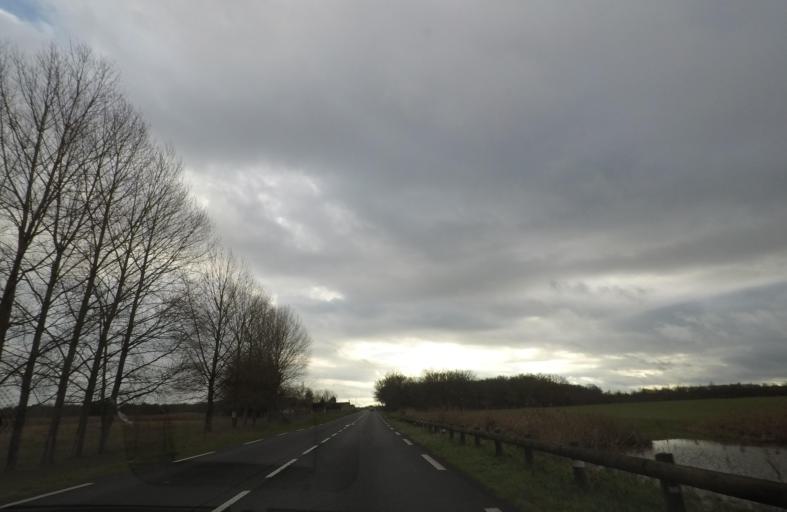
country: FR
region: Centre
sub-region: Departement du Loir-et-Cher
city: Soings-en-Sologne
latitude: 47.4352
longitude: 1.5582
